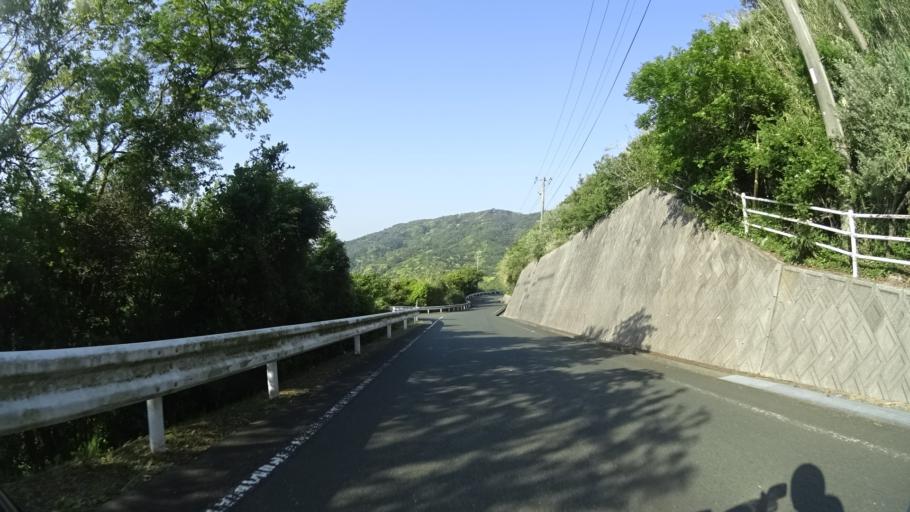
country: JP
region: Ehime
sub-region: Nishiuwa-gun
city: Ikata-cho
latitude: 33.3680
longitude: 132.0507
